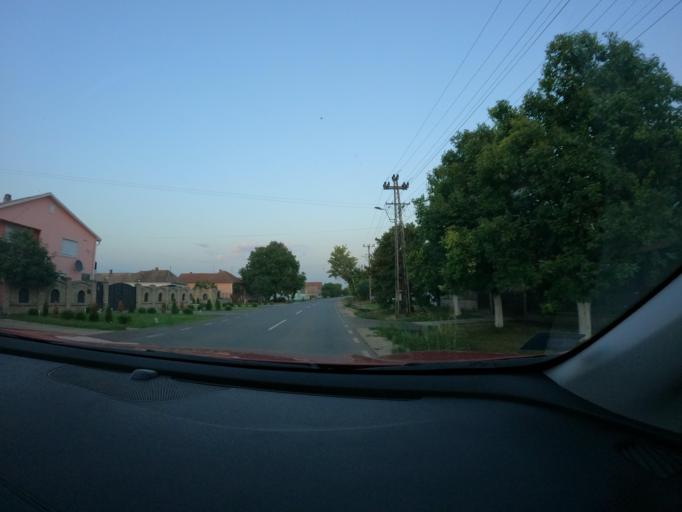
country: RS
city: Golubinci
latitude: 44.9865
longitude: 20.0508
